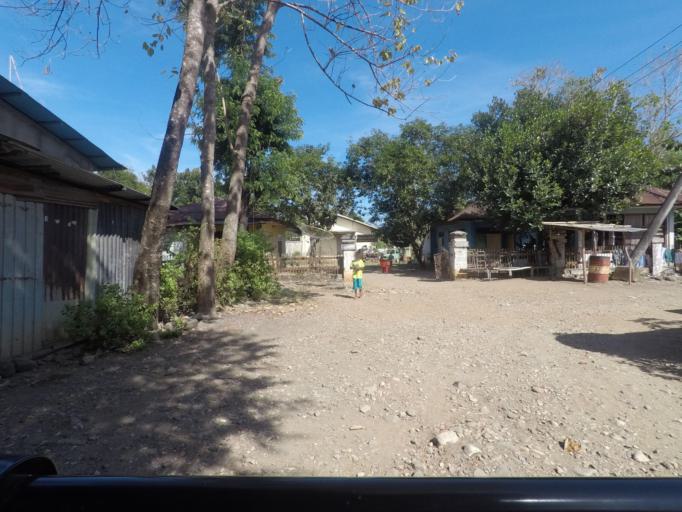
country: TL
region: Bobonaro
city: Maliana
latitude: -8.9925
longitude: 125.2168
